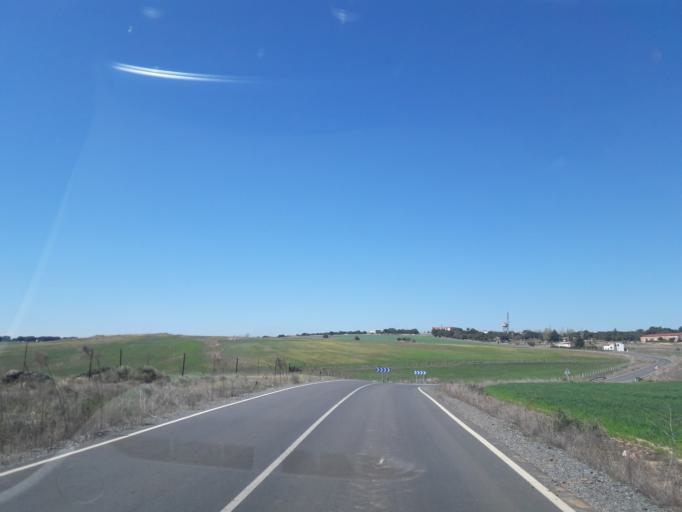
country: ES
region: Castille and Leon
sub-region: Provincia de Salamanca
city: Martinamor
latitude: 40.8092
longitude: -5.6198
